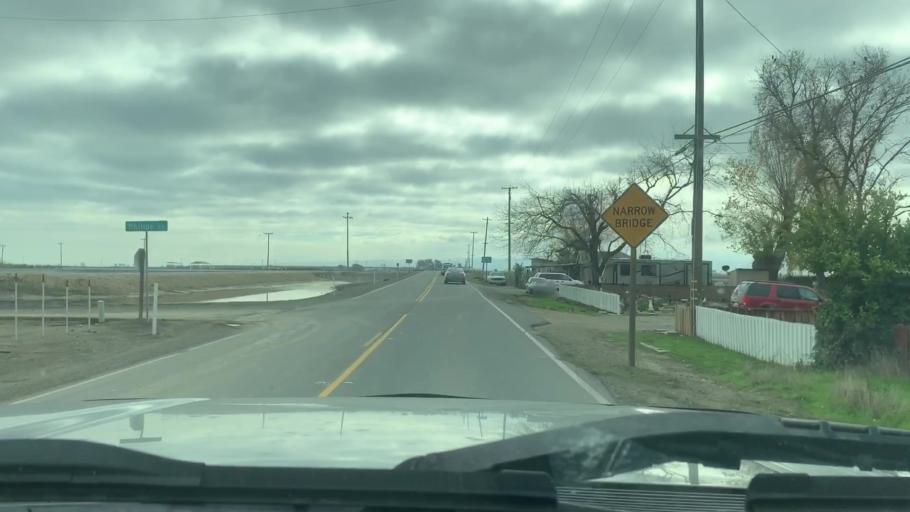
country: US
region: California
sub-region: Merced County
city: Los Banos
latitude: 37.0351
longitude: -120.8360
